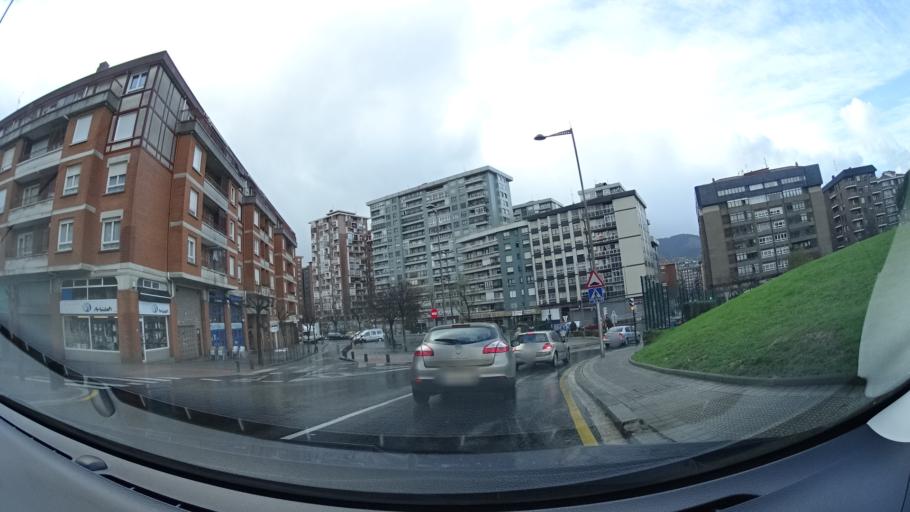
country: ES
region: Basque Country
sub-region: Bizkaia
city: Santutxu
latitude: 43.2566
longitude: -2.9105
